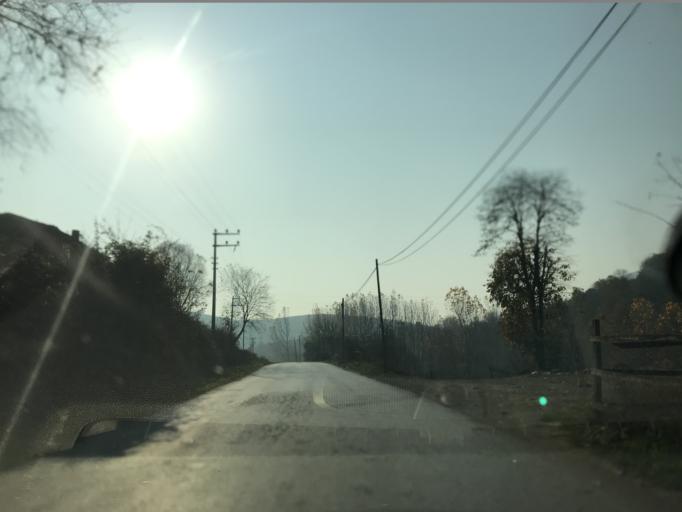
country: TR
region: Duzce
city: Cumayeri
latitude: 40.9067
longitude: 30.9510
